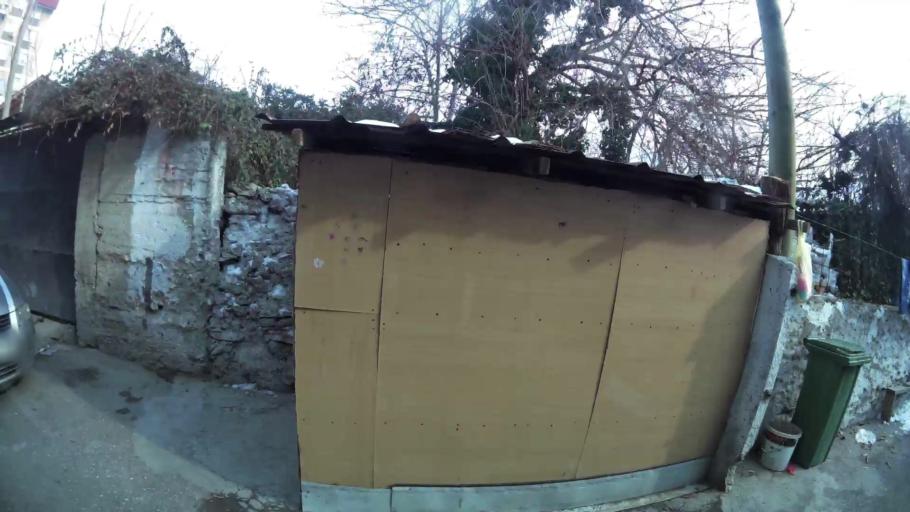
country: MK
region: Cair
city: Cair
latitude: 42.0123
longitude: 21.4384
